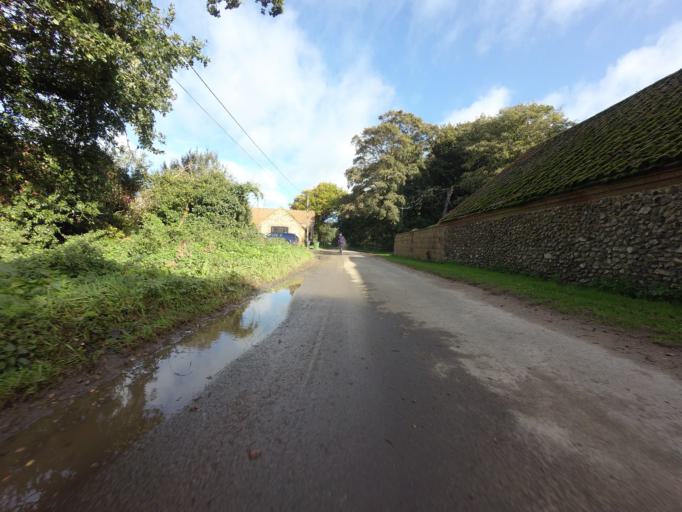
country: GB
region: England
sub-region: Norfolk
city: Dersingham
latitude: 52.8581
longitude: 0.6658
